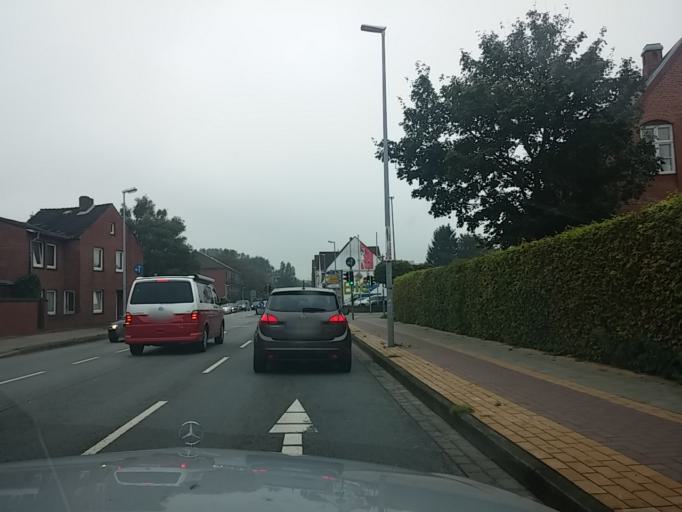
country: DE
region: Schleswig-Holstein
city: Husum
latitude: 54.4776
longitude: 9.0570
